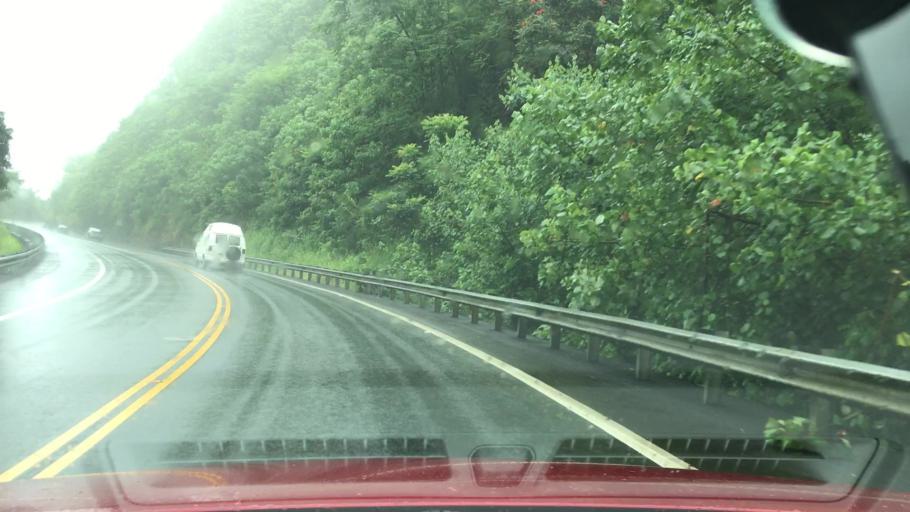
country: US
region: Hawaii
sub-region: Hawaii County
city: Pepeekeo
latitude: 19.9865
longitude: -155.2473
